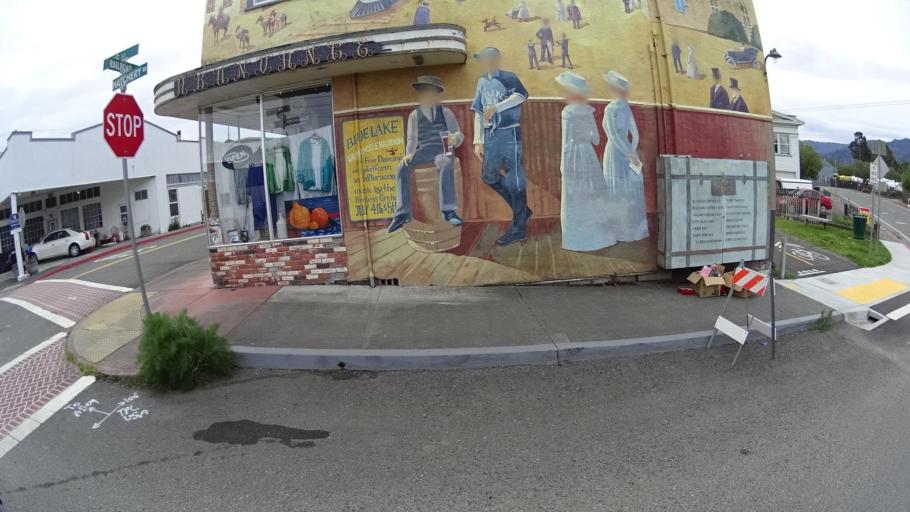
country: US
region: California
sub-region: Humboldt County
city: Blue Lake
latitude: 40.8809
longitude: -123.9900
